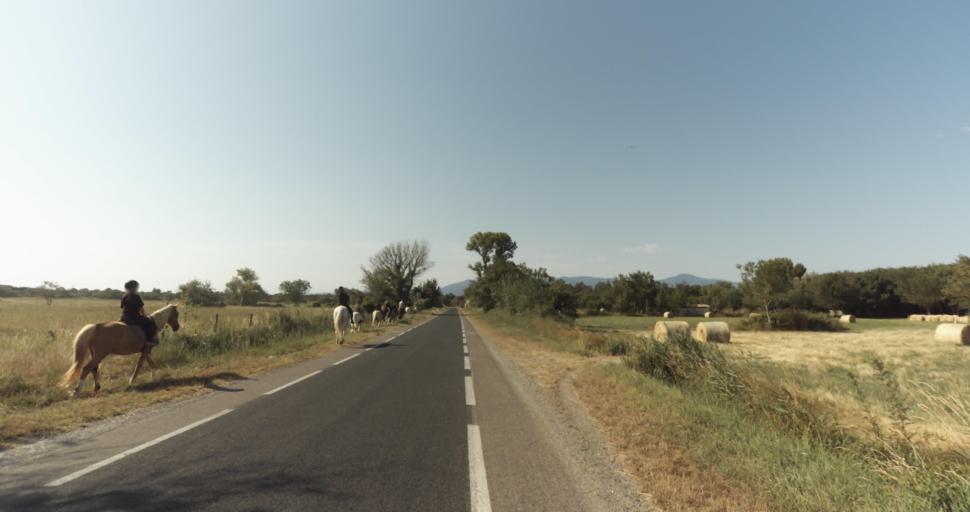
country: FR
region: Languedoc-Roussillon
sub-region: Departement des Pyrenees-Orientales
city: Saint-Cyprien-Plage
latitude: 42.6296
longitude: 3.0188
